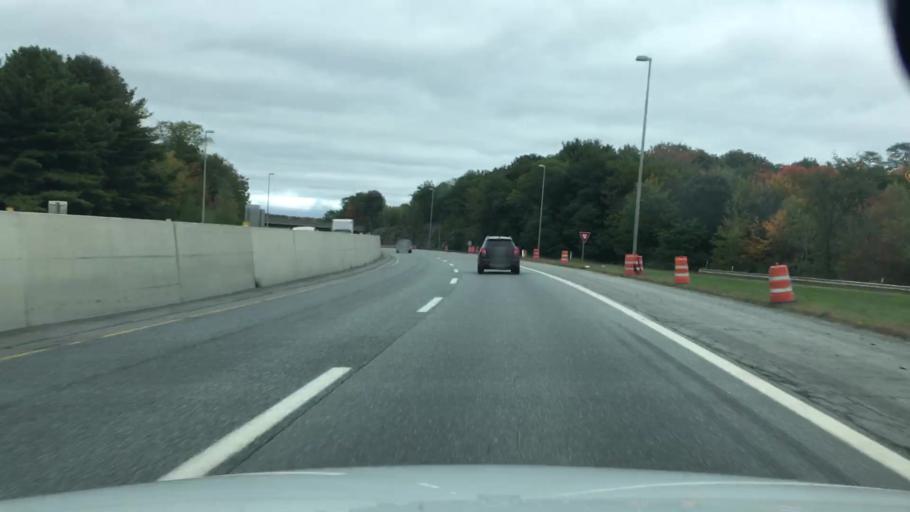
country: US
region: Maine
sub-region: Penobscot County
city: Bangor
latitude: 44.8194
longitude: -68.7729
